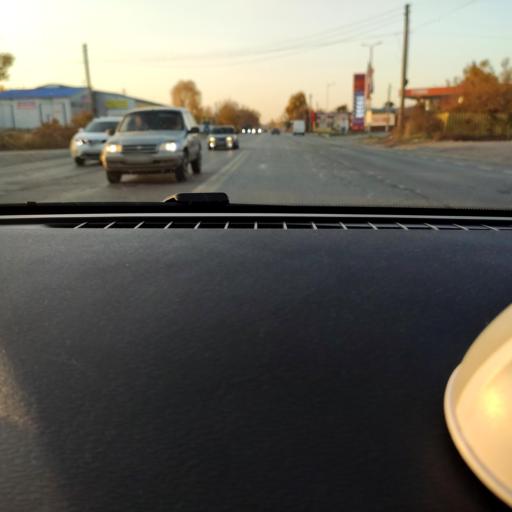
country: RU
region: Samara
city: Petra-Dubrava
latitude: 53.2641
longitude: 50.2861
